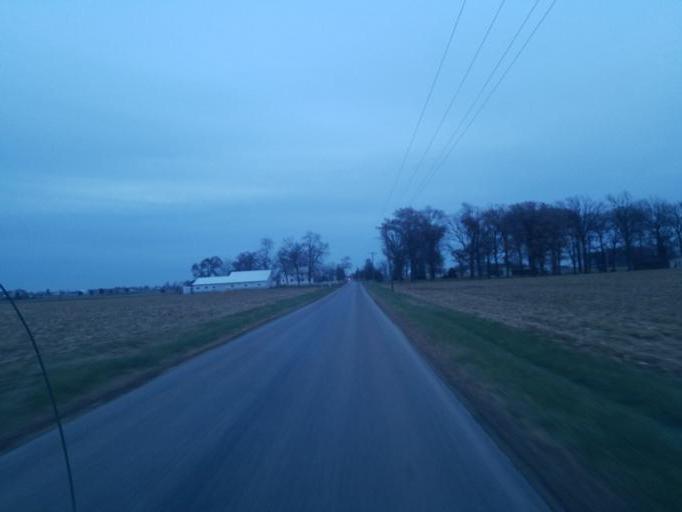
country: US
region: Indiana
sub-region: Adams County
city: Berne
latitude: 40.7304
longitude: -84.9688
